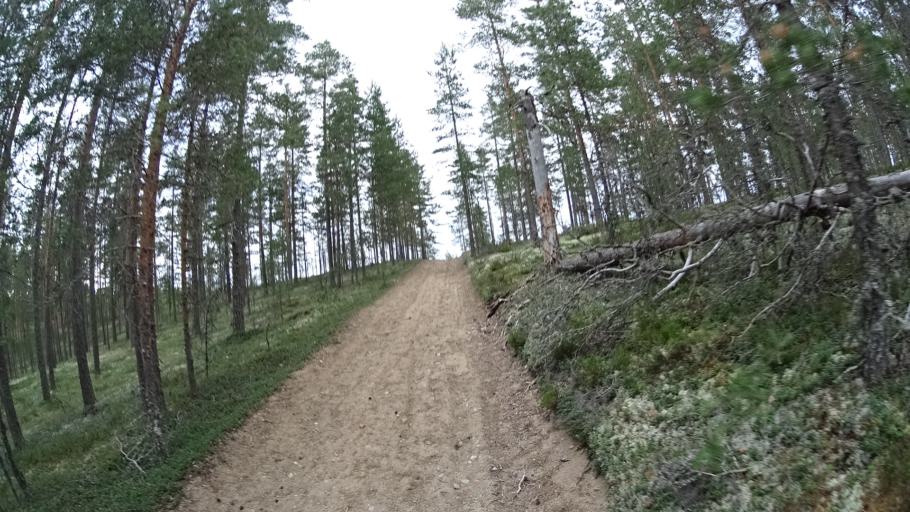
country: FI
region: Satakunta
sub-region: Pohjois-Satakunta
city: Jaemijaervi
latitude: 61.7692
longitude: 22.7910
